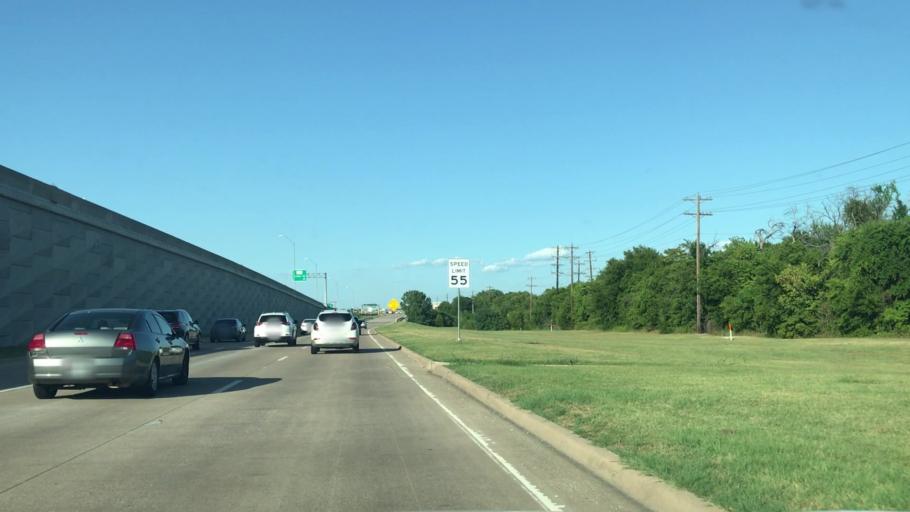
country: US
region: Texas
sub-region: Collin County
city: Frisco
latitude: 33.1188
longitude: -96.7504
